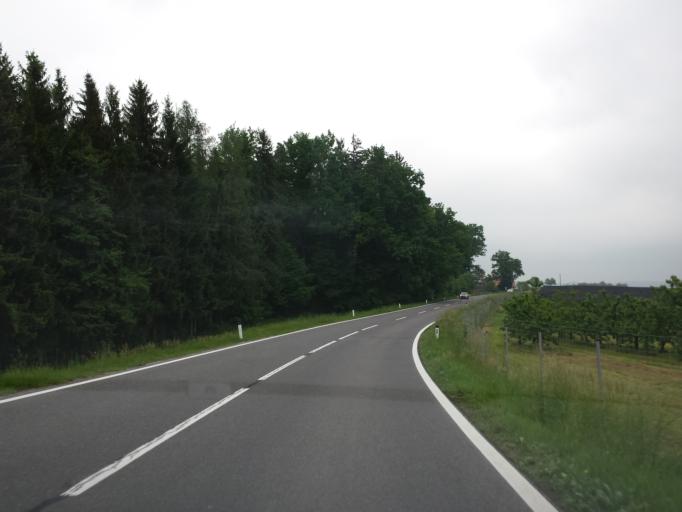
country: AT
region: Styria
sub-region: Politischer Bezirk Weiz
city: Mitterdorf an der Raab
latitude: 47.1695
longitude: 15.5875
